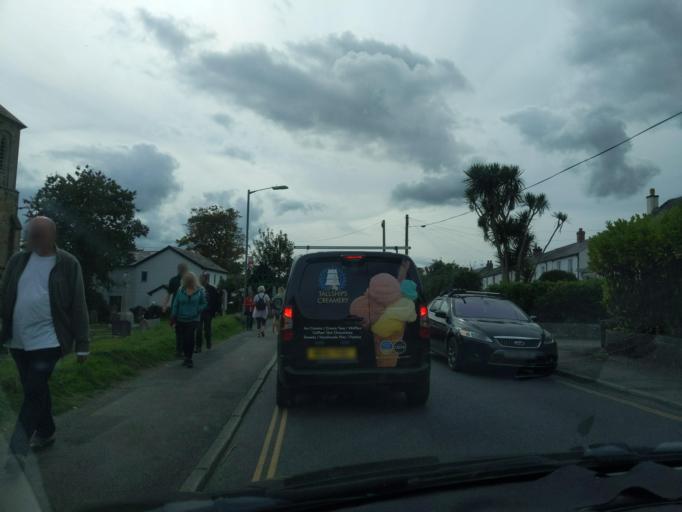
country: GB
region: England
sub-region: Cornwall
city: St Austell
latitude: 50.3350
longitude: -4.7609
